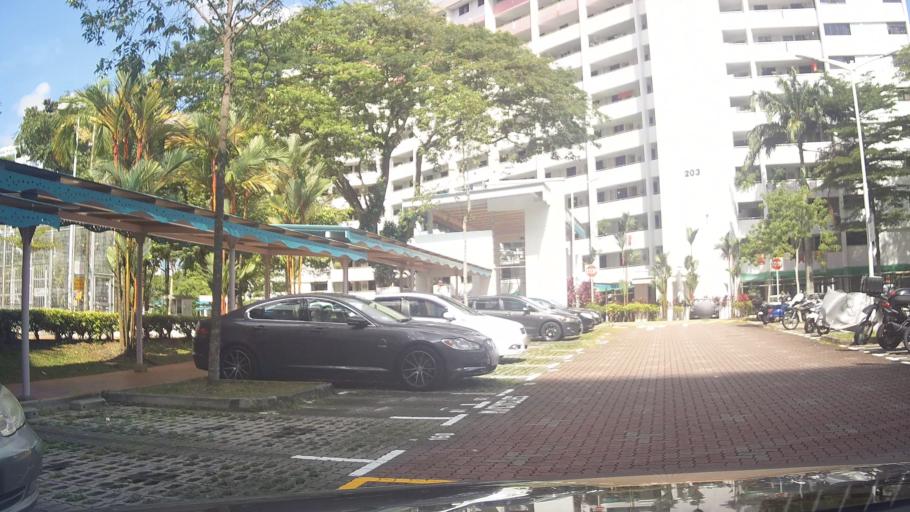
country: MY
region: Johor
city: Johor Bahru
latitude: 1.4434
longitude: 103.7751
